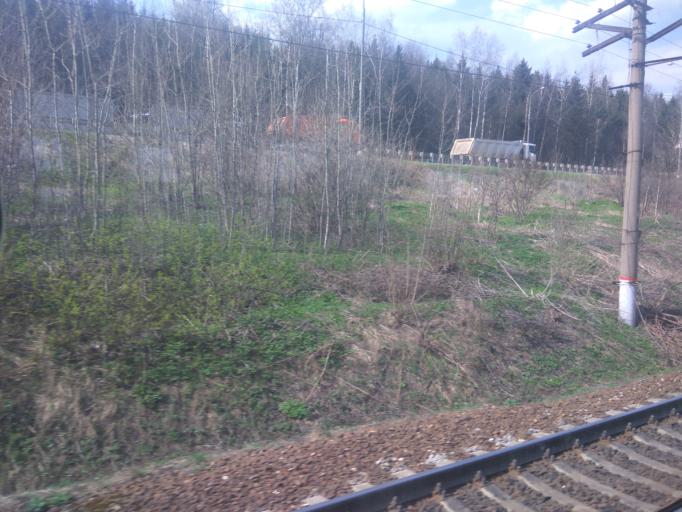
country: RU
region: Moskovskaya
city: Iksha
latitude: 56.1884
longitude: 37.5213
